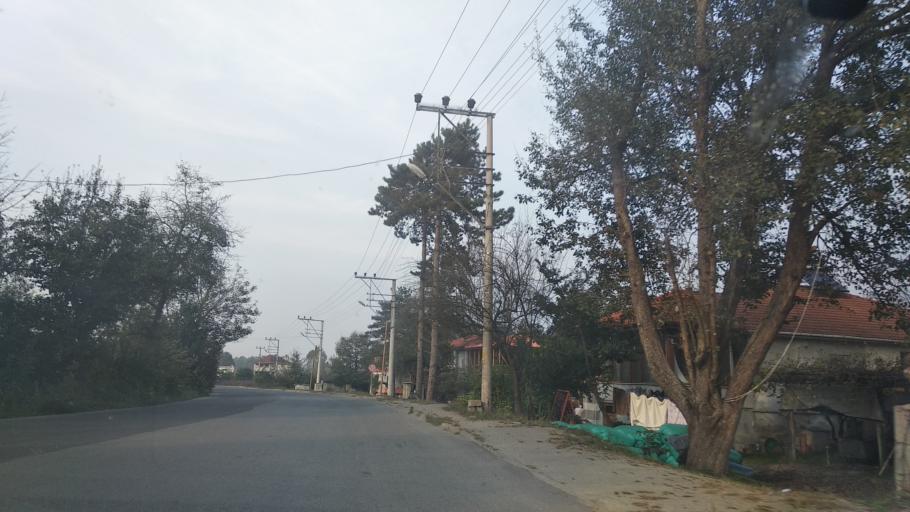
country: TR
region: Duzce
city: Duzce
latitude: 40.8085
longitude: 31.1786
